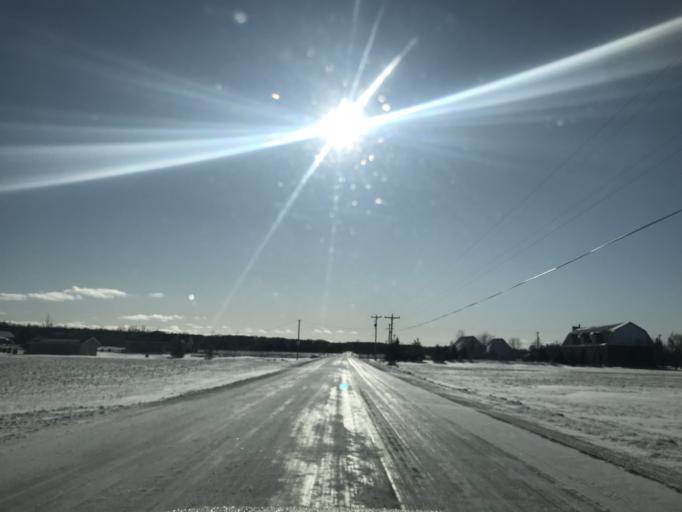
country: US
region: Wisconsin
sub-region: Door County
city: Sturgeon Bay
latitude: 44.8366
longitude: -87.5040
